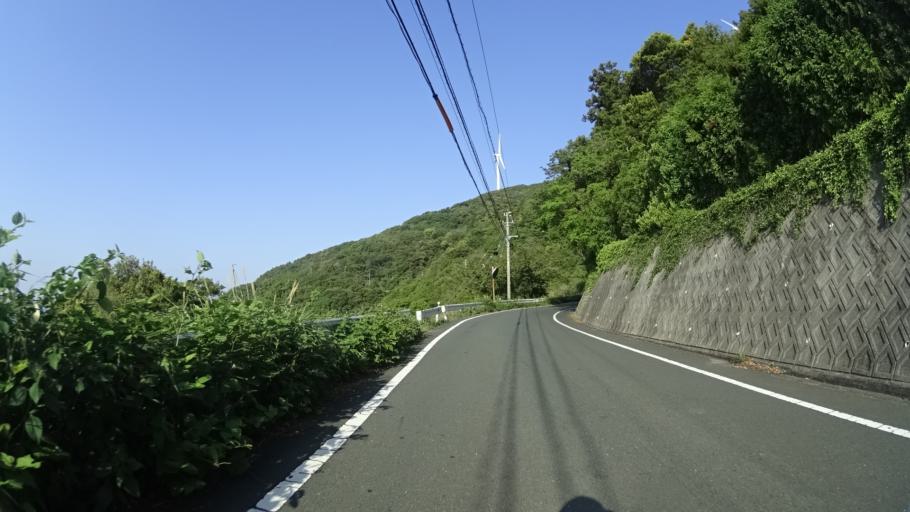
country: JP
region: Ehime
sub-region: Nishiuwa-gun
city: Ikata-cho
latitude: 33.3877
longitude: 132.0912
